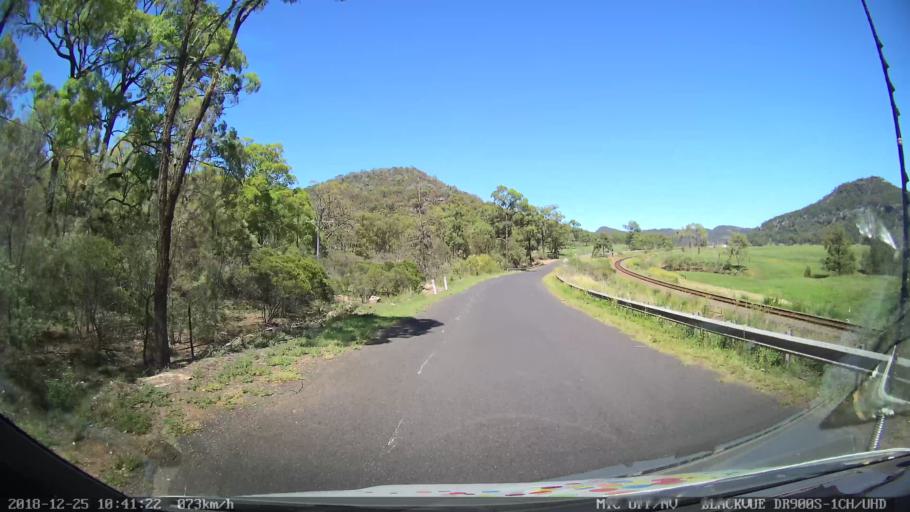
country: AU
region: New South Wales
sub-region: Upper Hunter Shire
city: Merriwa
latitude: -32.4159
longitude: 150.3364
